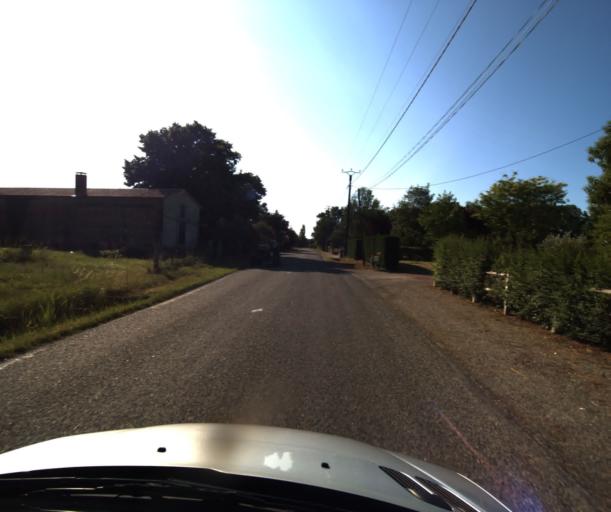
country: FR
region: Midi-Pyrenees
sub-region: Departement du Tarn-et-Garonne
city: Saint-Porquier
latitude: 44.0703
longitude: 1.1997
